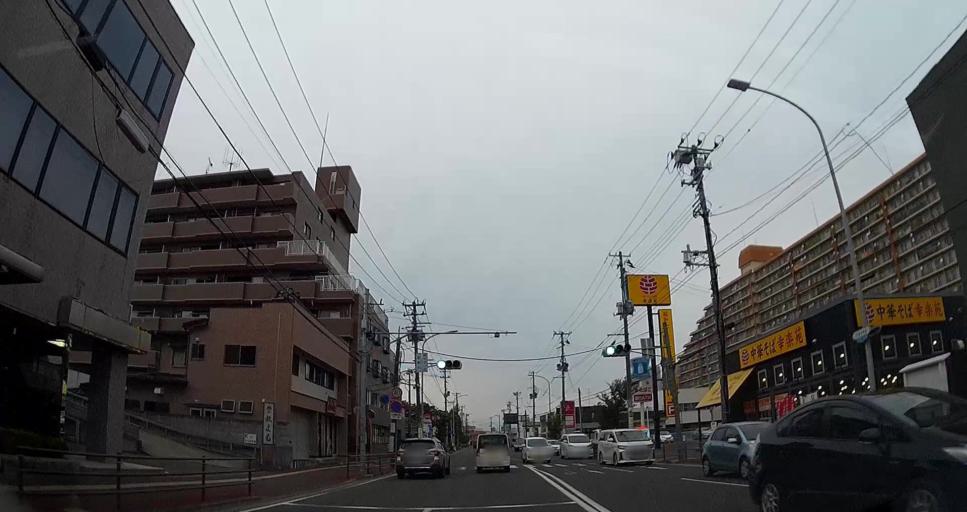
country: JP
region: Miyagi
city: Sendai
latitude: 38.2268
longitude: 140.8953
